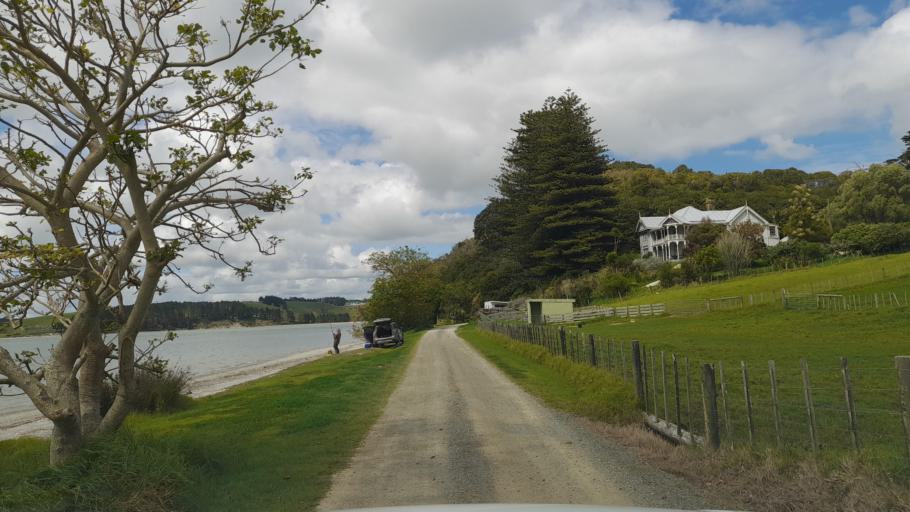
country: NZ
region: Auckland
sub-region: Auckland
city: Wellsford
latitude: -36.2211
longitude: 174.3205
